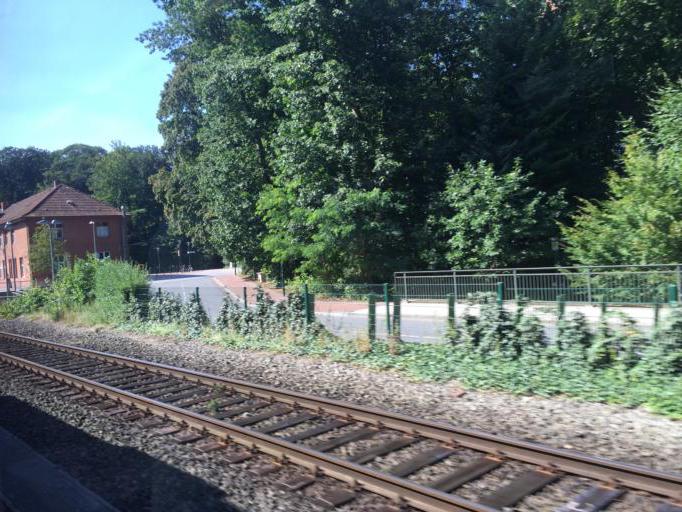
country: DE
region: Schleswig-Holstein
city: Bad Schwartau
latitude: 53.9170
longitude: 10.7037
